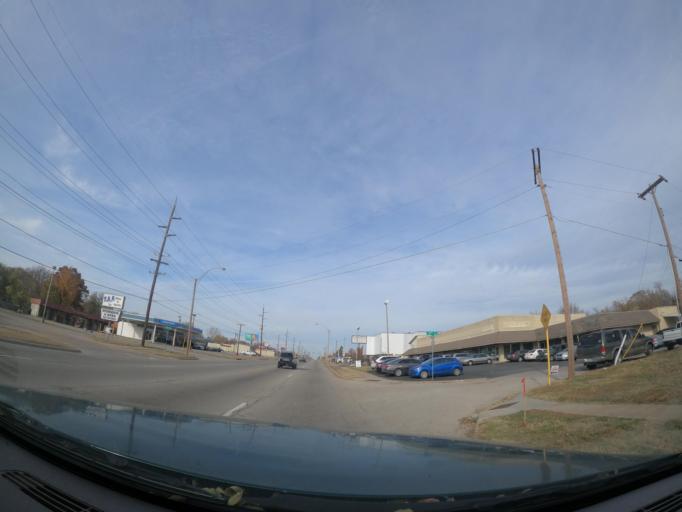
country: US
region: Oklahoma
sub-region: Tulsa County
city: Turley
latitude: 36.2232
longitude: -95.9755
